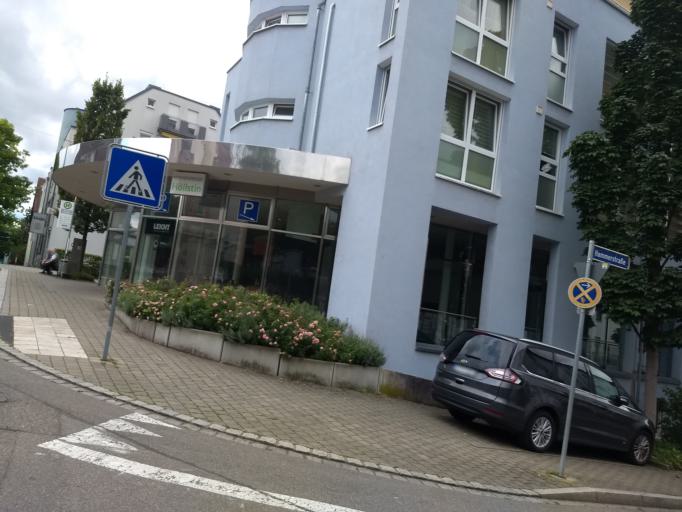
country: CH
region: Basel-City
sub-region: Basel-Stadt
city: Riehen
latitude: 47.5964
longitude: 7.6559
